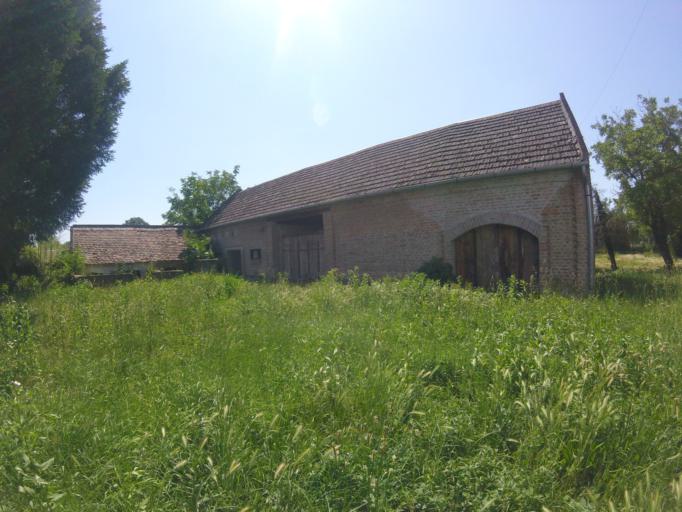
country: HU
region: Baranya
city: Sellye
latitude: 45.9020
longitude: 17.8578
